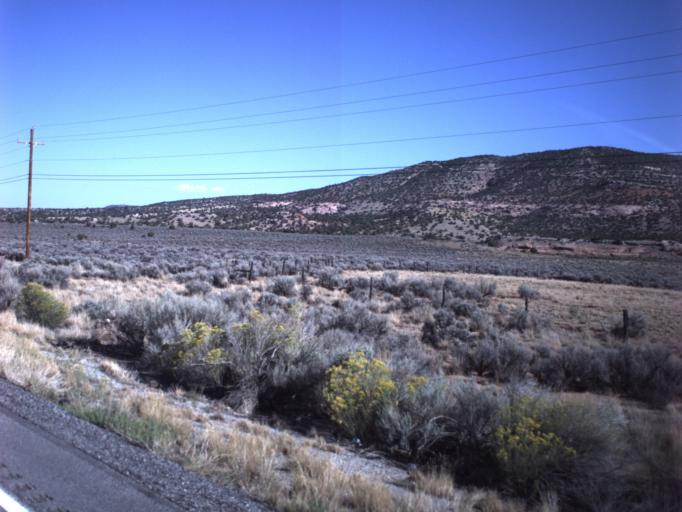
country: US
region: Utah
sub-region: Grand County
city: Moab
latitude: 38.2950
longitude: -109.3857
